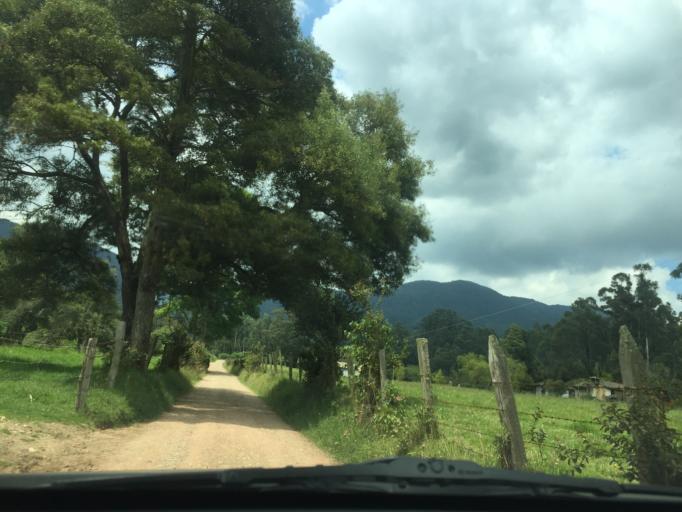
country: CO
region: Cundinamarca
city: Cogua
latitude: 5.0558
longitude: -73.9975
